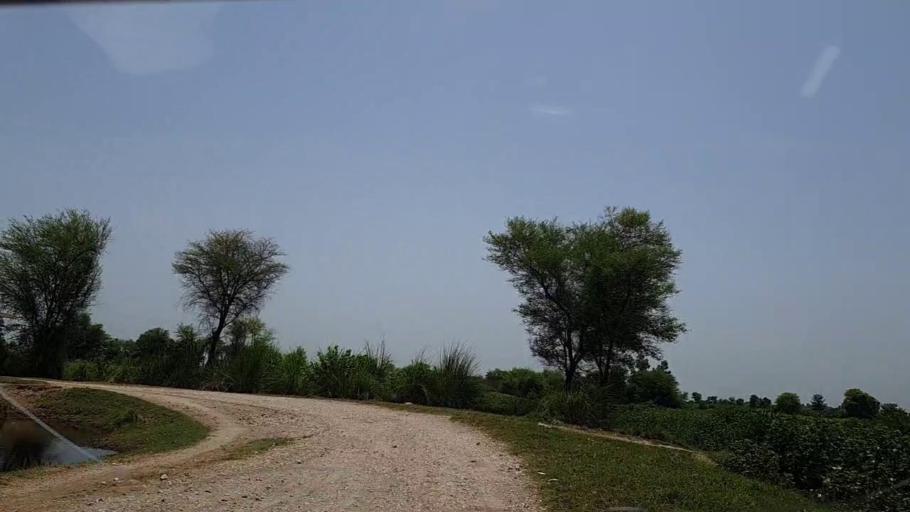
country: PK
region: Sindh
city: Tharu Shah
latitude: 26.9263
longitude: 68.0410
